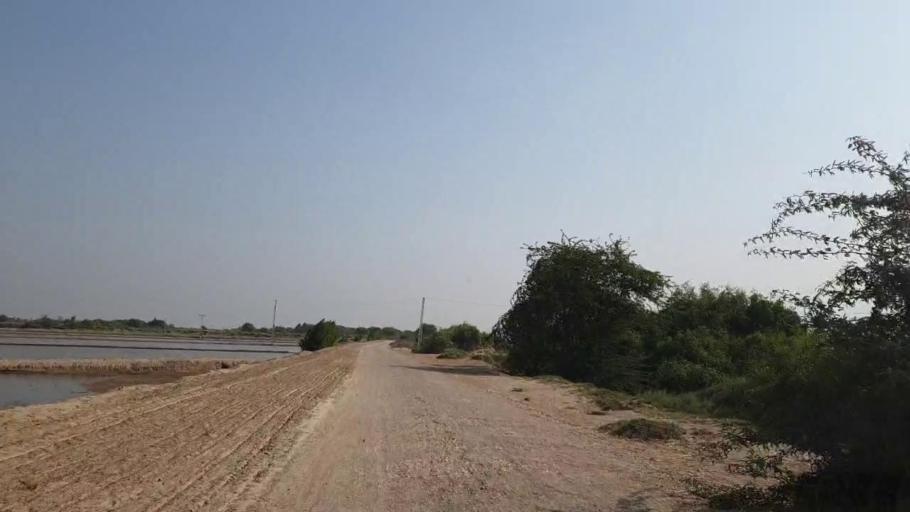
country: PK
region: Sindh
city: Bulri
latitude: 24.9340
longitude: 68.3676
